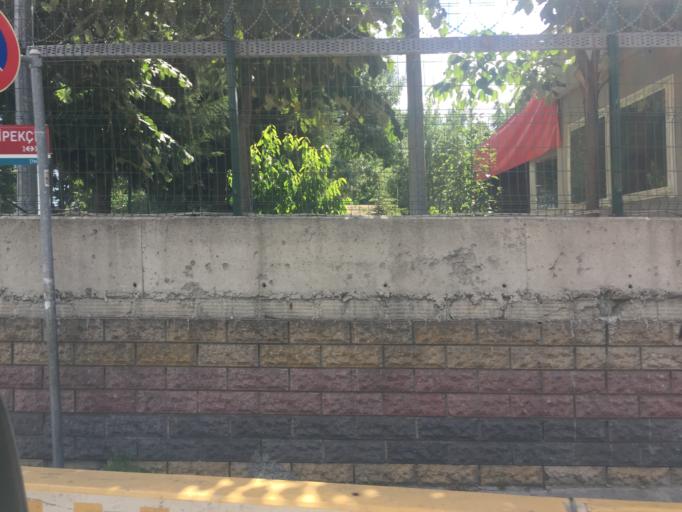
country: TR
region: Istanbul
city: merter keresteciler
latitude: 41.0334
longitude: 28.9123
